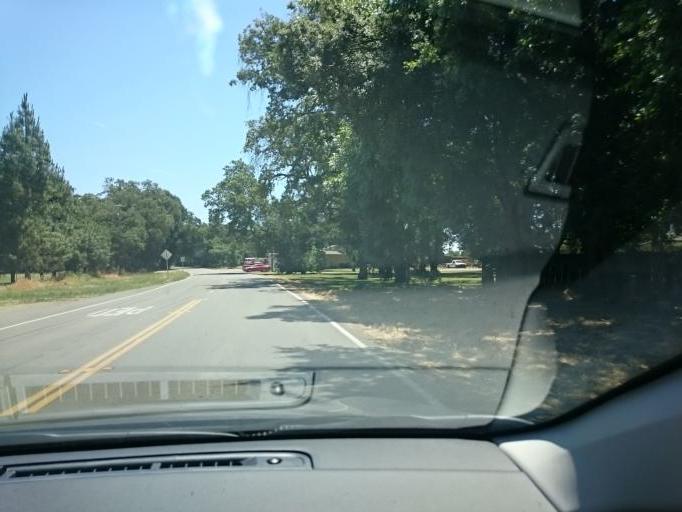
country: US
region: California
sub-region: San Joaquin County
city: Thornton
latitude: 38.2240
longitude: -121.4223
